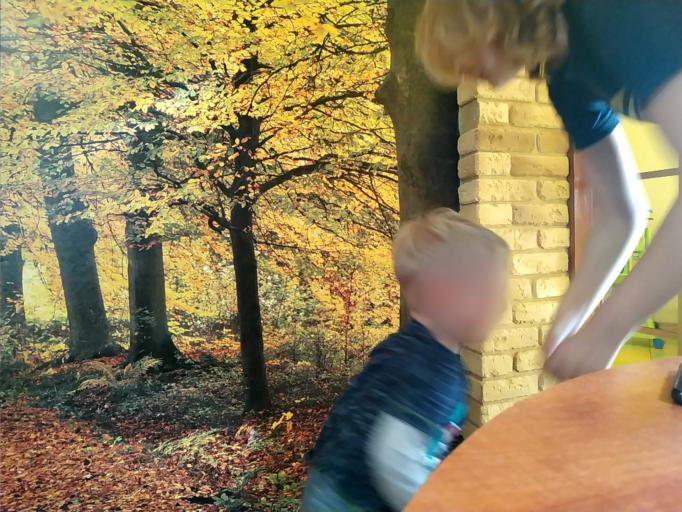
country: RU
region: Novgorod
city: Parfino
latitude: 57.7998
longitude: 31.6149
